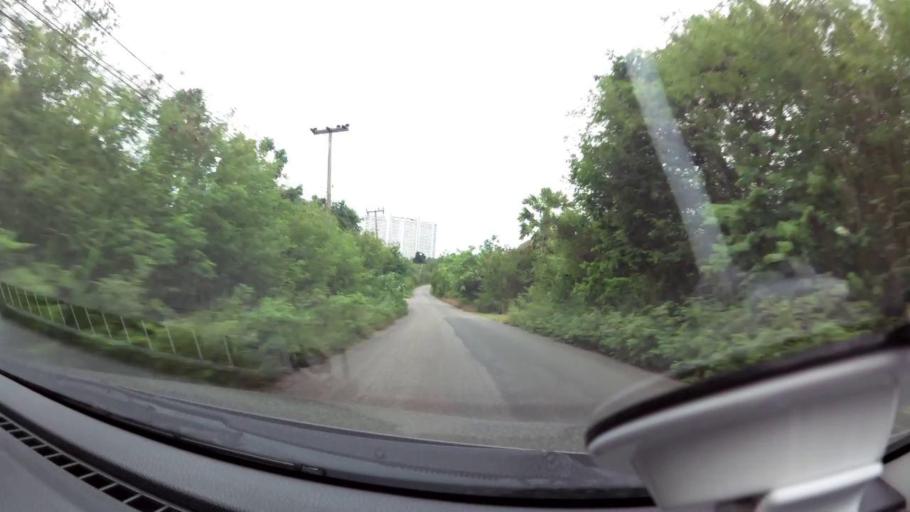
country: TH
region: Prachuap Khiri Khan
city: Pran Buri
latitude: 12.4377
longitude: 99.9722
